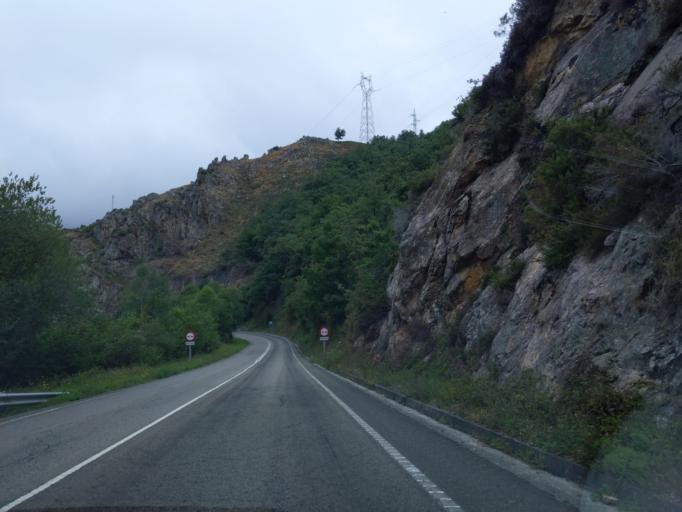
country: ES
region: Asturias
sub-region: Province of Asturias
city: Pola de Laviana
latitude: 43.2273
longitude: -5.4700
